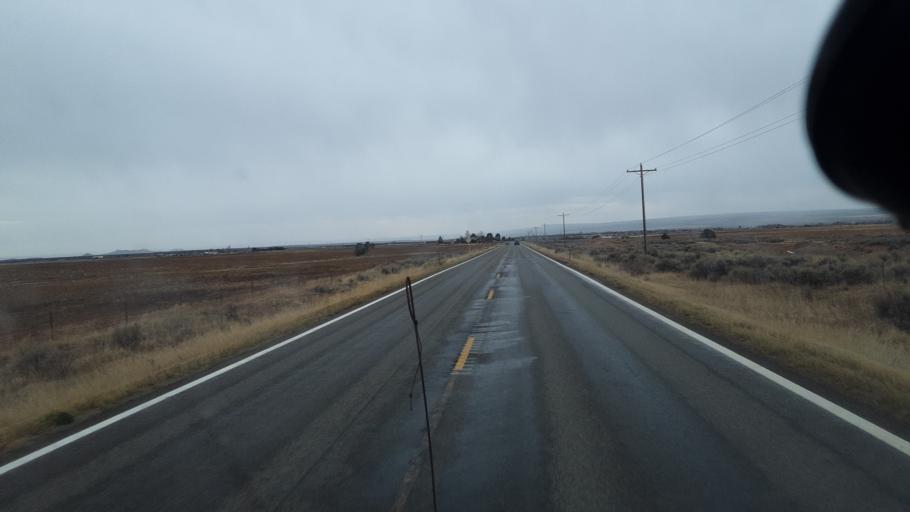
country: US
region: Colorado
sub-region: Montezuma County
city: Mancos
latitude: 37.1401
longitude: -108.1256
